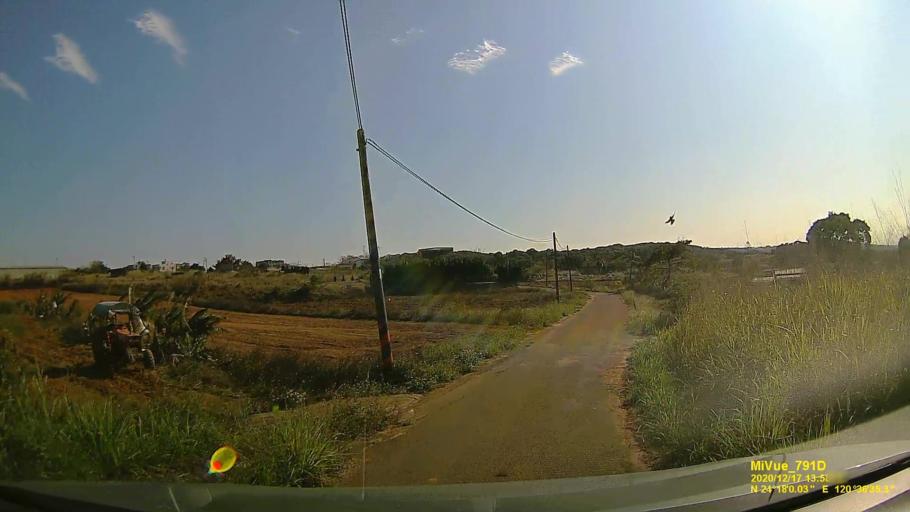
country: TW
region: Taiwan
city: Fengyuan
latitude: 24.3000
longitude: 120.6098
